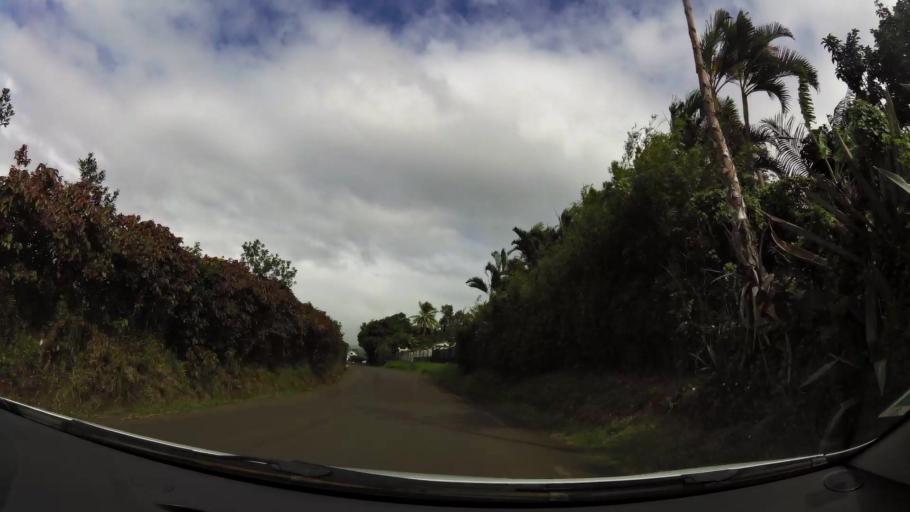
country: RE
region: Reunion
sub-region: Reunion
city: Sainte-Marie
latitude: -20.9009
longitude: 55.5697
